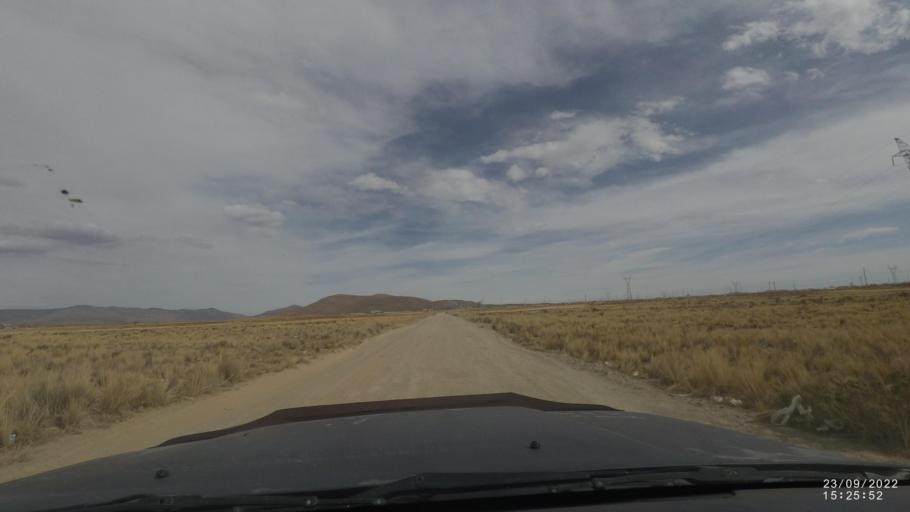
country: BO
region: Oruro
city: Oruro
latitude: -17.9490
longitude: -67.0393
